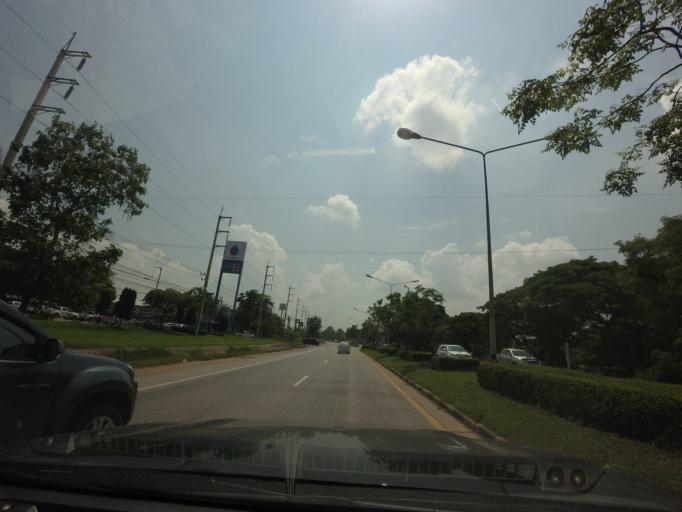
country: TH
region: Uttaradit
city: Uttaradit
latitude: 17.6053
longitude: 100.1235
